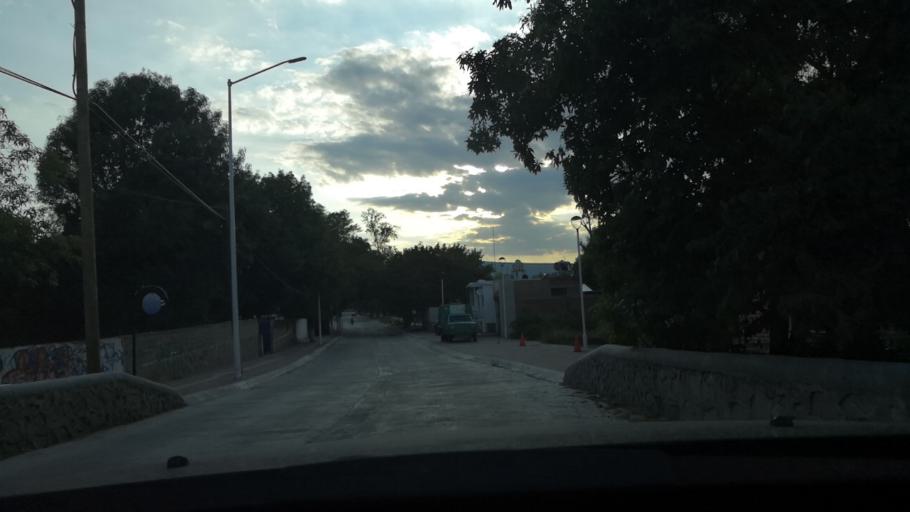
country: MX
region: Guanajuato
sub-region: San Francisco del Rincon
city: Estacion de San Francisco
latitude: 21.0264
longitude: -101.8352
